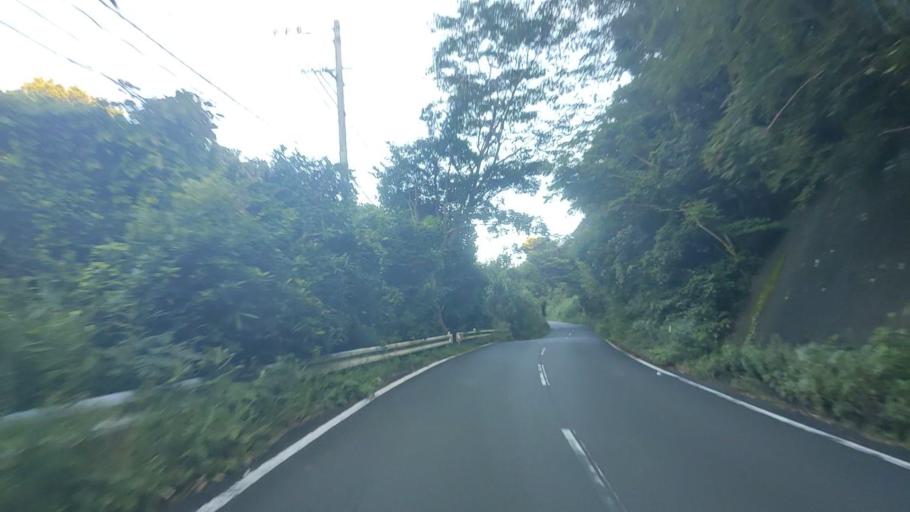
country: JP
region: Mie
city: Ise
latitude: 34.2685
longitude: 136.7687
